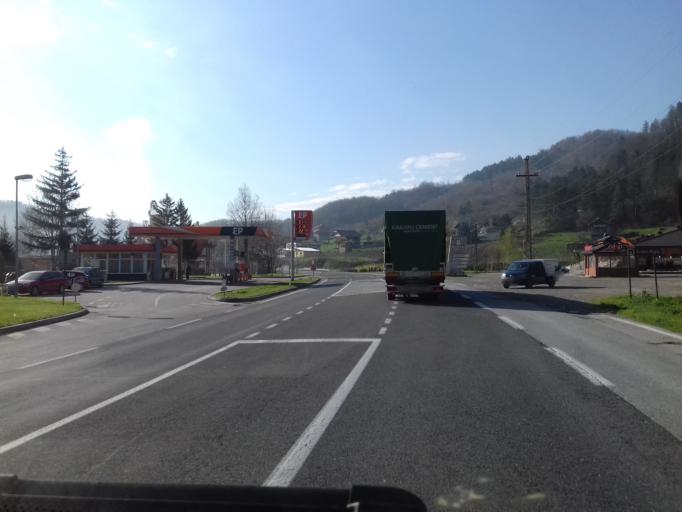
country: BA
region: Federation of Bosnia and Herzegovina
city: Maglaj
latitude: 44.5779
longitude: 18.0950
